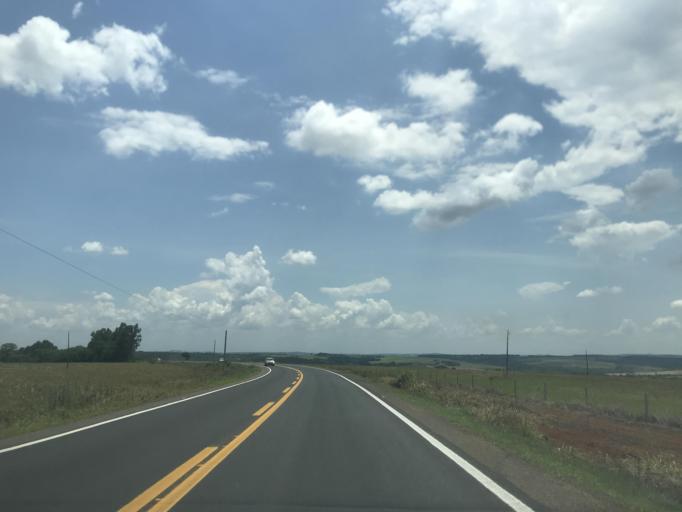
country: BR
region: Goias
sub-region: Bela Vista De Goias
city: Bela Vista de Goias
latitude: -17.1037
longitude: -48.6637
